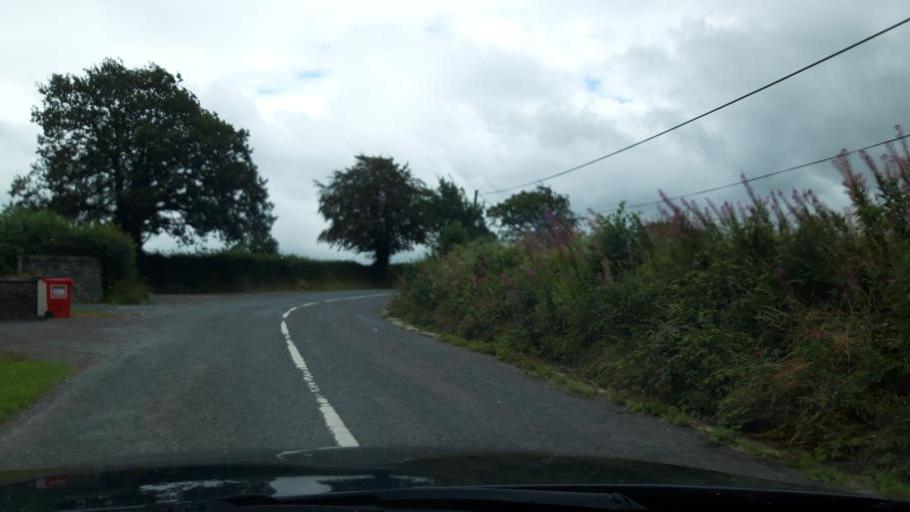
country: IE
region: Munster
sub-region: County Cork
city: Castlemartyr
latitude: 52.1318
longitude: -7.9955
